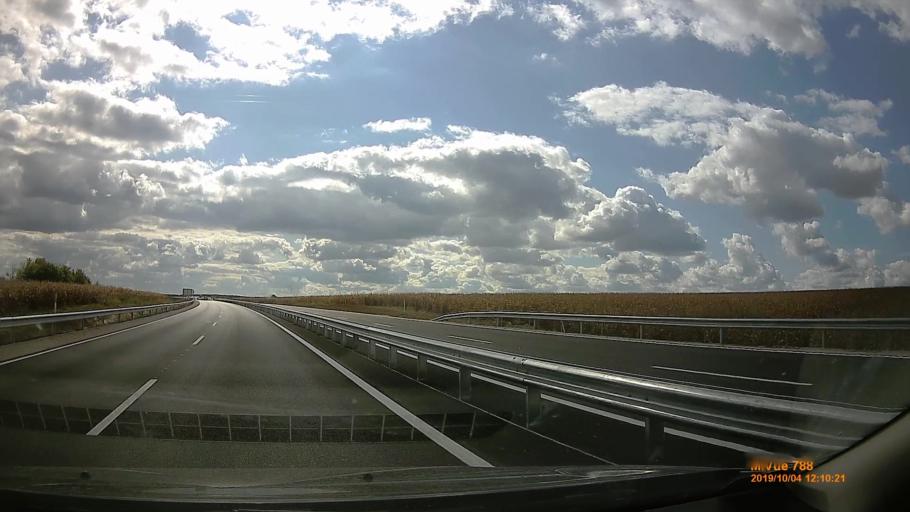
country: HU
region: Somogy
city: Kaposvar
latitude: 46.5076
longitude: 17.8087
